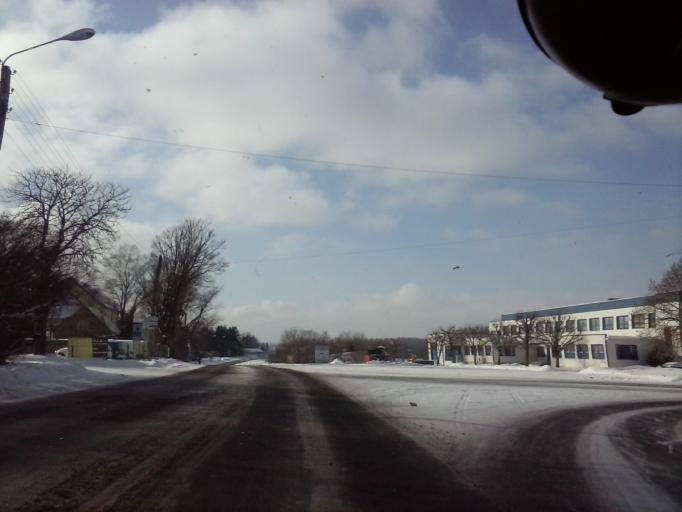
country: EE
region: Viljandimaa
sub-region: Viljandi linn
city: Viljandi
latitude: 58.3579
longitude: 25.5663
